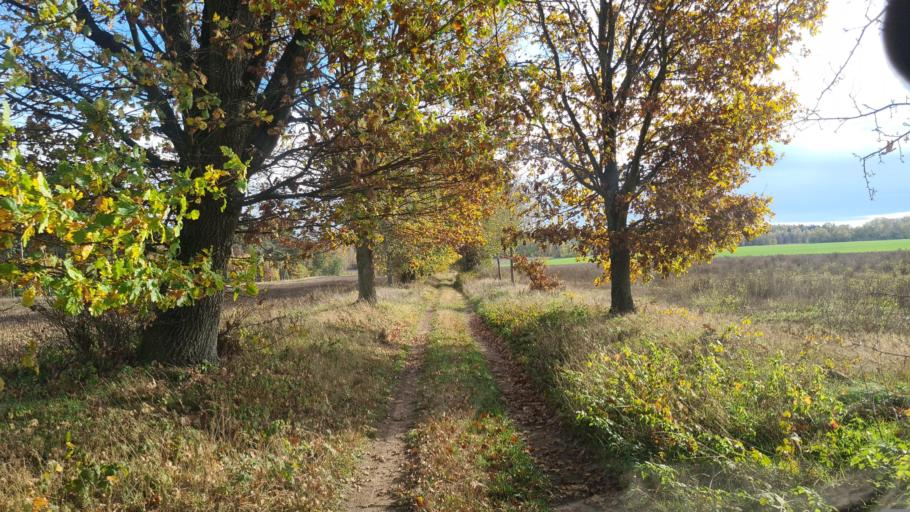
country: DE
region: Brandenburg
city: Wiesenburg
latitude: 52.0820
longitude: 12.4595
